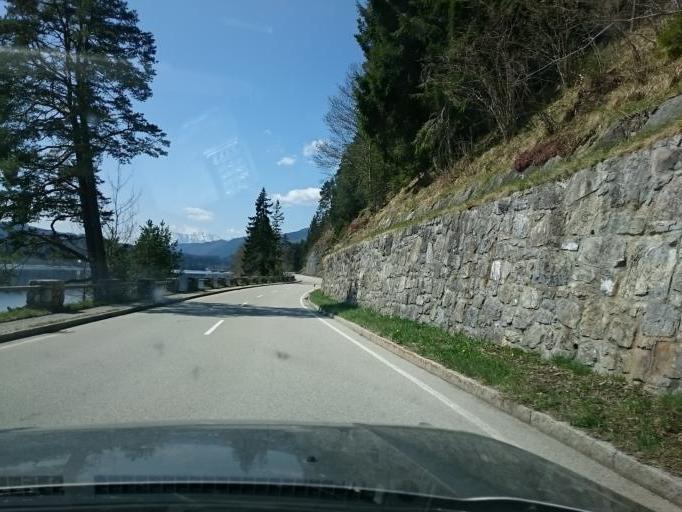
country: DE
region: Bavaria
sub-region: Upper Bavaria
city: Schlehdorf
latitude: 47.6009
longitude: 11.3285
